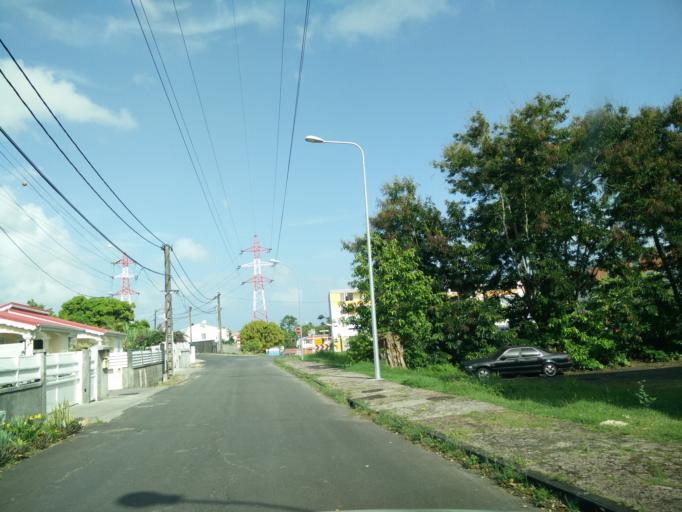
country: GP
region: Guadeloupe
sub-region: Guadeloupe
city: Les Abymes
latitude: 16.2540
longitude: -61.5165
